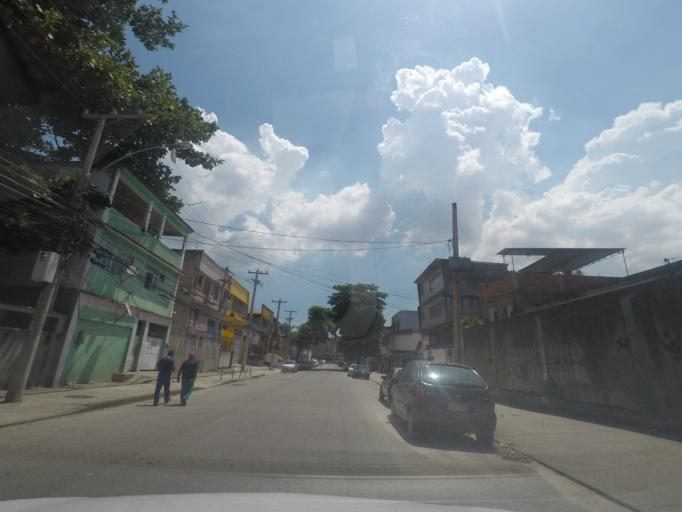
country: BR
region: Rio de Janeiro
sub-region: Rio De Janeiro
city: Rio de Janeiro
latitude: -22.8762
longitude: -43.2549
